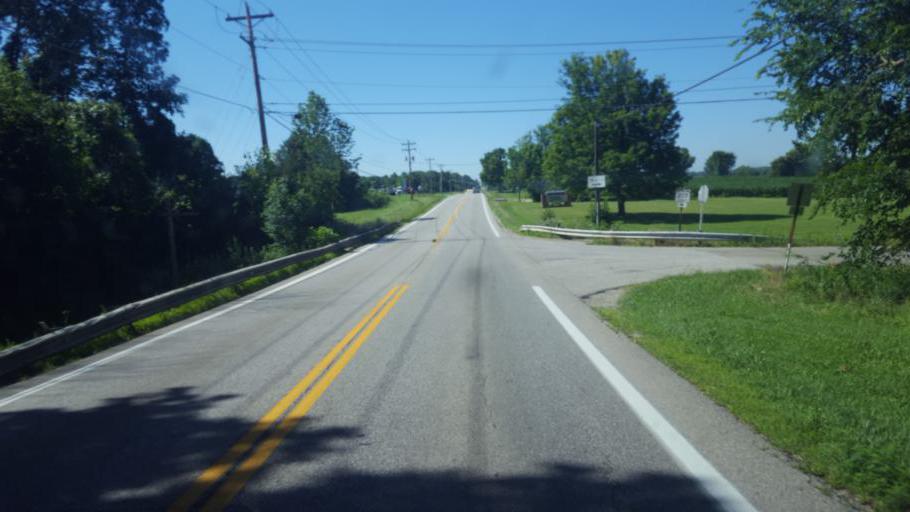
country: US
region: Ohio
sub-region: Morrow County
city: Cardington
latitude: 40.3902
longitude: -82.8277
